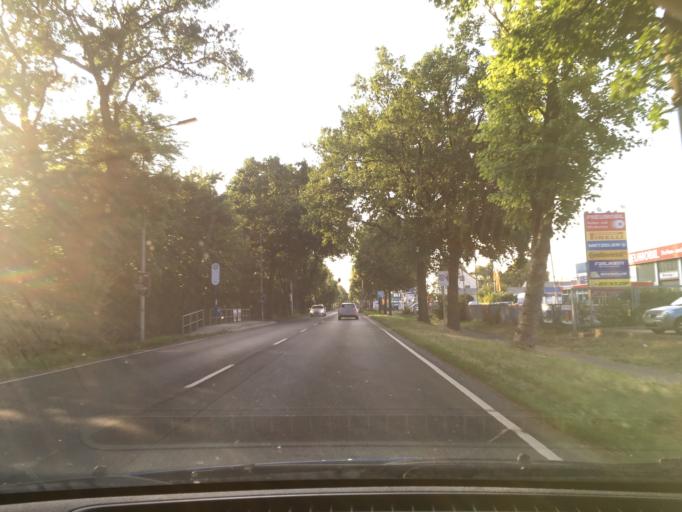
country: DE
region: Lower Saxony
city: Celle
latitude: 52.6085
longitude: 10.1008
